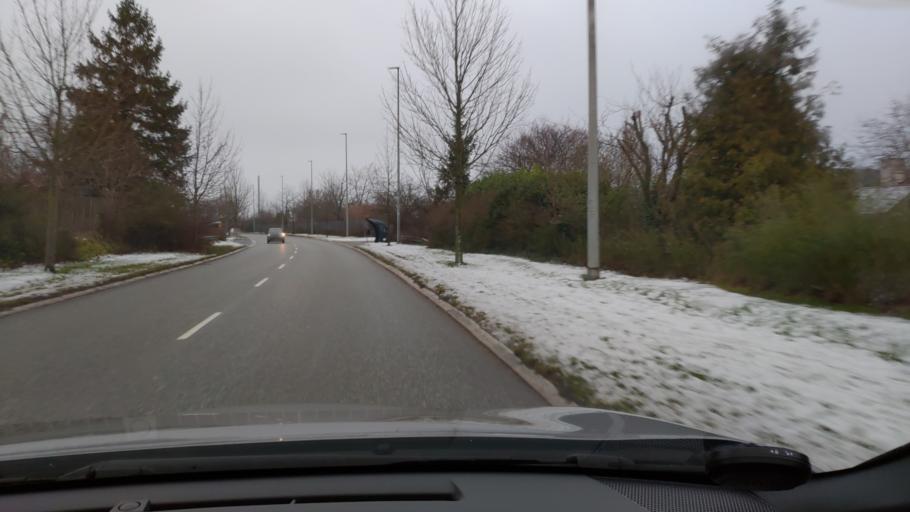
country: DK
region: Zealand
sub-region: Greve Kommune
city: Greve
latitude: 55.5811
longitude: 12.2678
